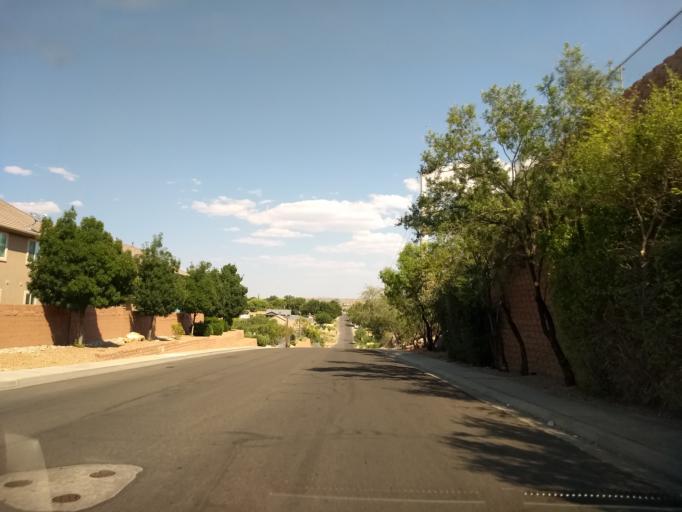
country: US
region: Utah
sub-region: Washington County
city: Washington
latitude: 37.1278
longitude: -113.5173
